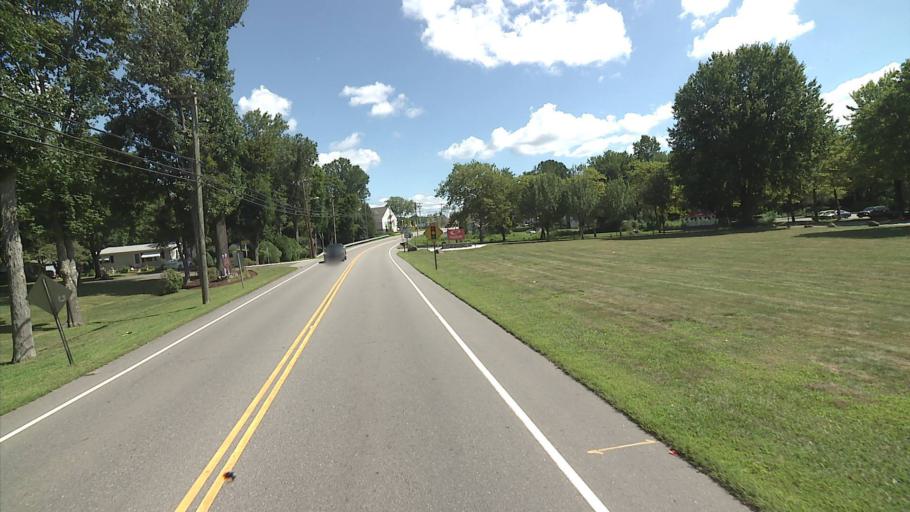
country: US
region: Connecticut
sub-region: Middlesex County
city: Saybrook Manor
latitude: 41.2852
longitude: -72.4195
